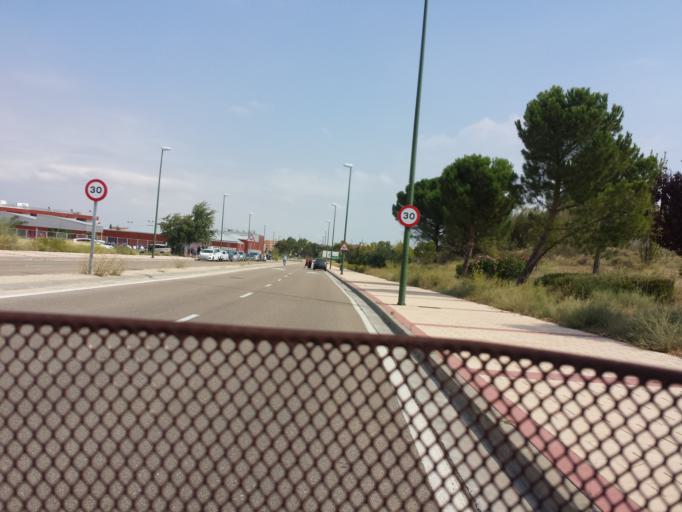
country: ES
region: Aragon
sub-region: Provincia de Zaragoza
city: Montecanal
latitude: 41.6335
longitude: -0.9410
